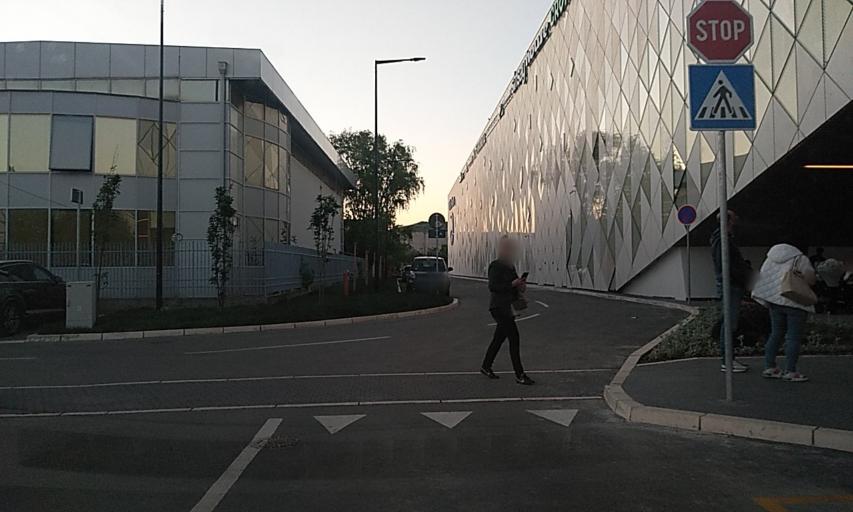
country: RS
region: Central Serbia
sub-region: Nisavski Okrug
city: Nis
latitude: 43.3244
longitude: 21.9101
